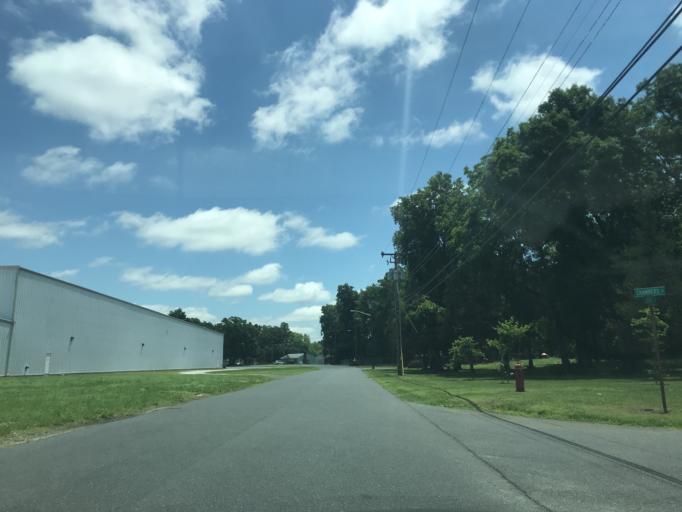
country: US
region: Maryland
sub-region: Caroline County
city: Federalsburg
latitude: 38.6940
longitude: -75.7658
